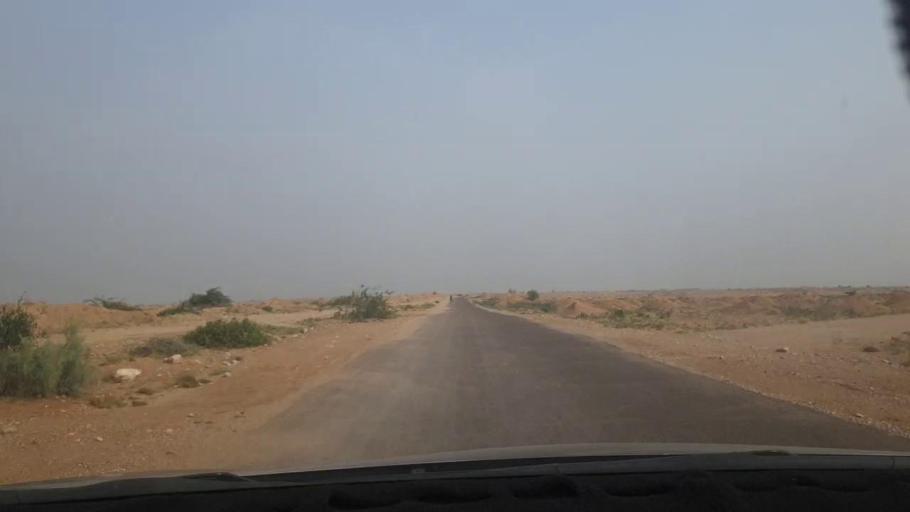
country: PK
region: Sindh
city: Matiari
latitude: 25.5781
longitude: 68.3184
